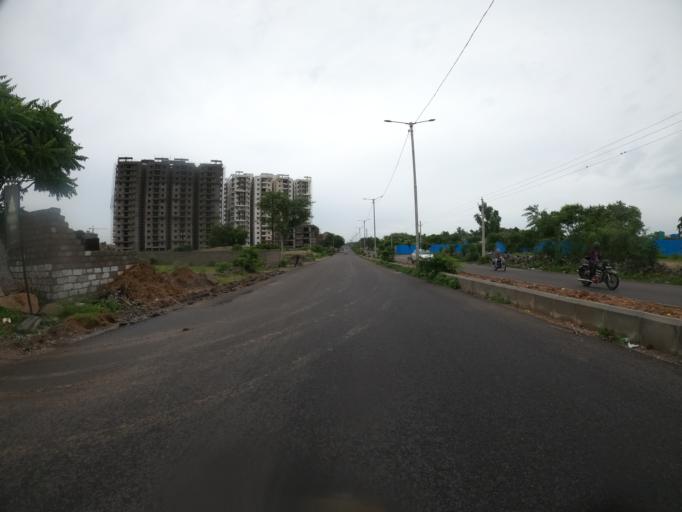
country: IN
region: Telangana
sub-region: Rangareddi
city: Kukatpalli
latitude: 17.4618
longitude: 78.3900
